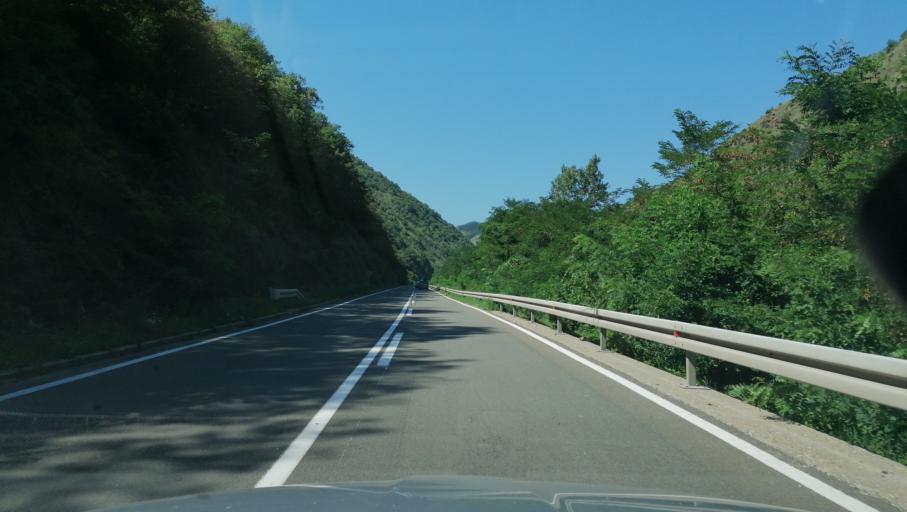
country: RS
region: Central Serbia
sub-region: Raski Okrug
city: Kraljevo
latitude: 43.6032
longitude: 20.5577
